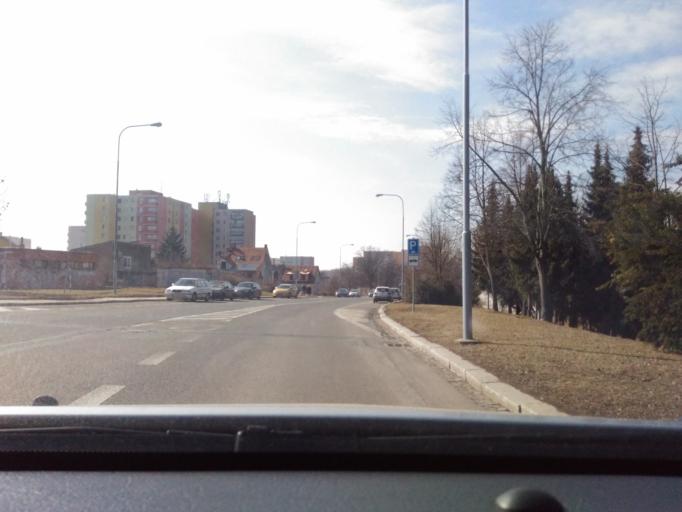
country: CZ
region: South Moravian
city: Moravany
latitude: 49.1704
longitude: 16.5806
